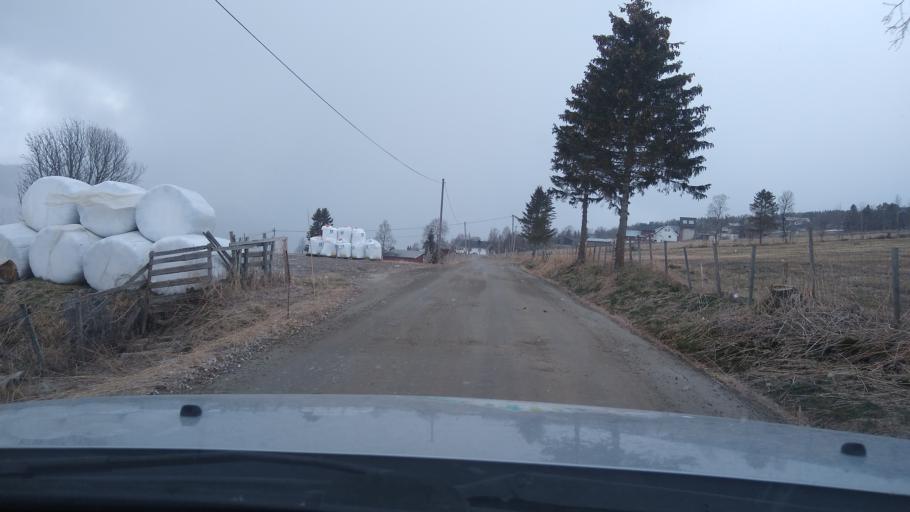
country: NO
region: Oppland
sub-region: Oyer
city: Tretten
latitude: 61.4604
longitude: 10.3309
